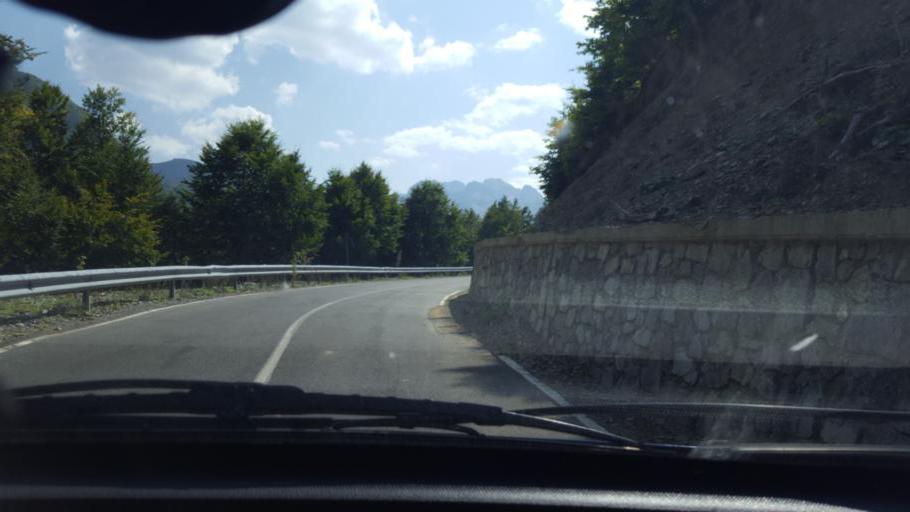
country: AL
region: Kukes
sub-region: Rrethi i Tropojes
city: Valbone
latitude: 42.5381
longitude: 19.7204
